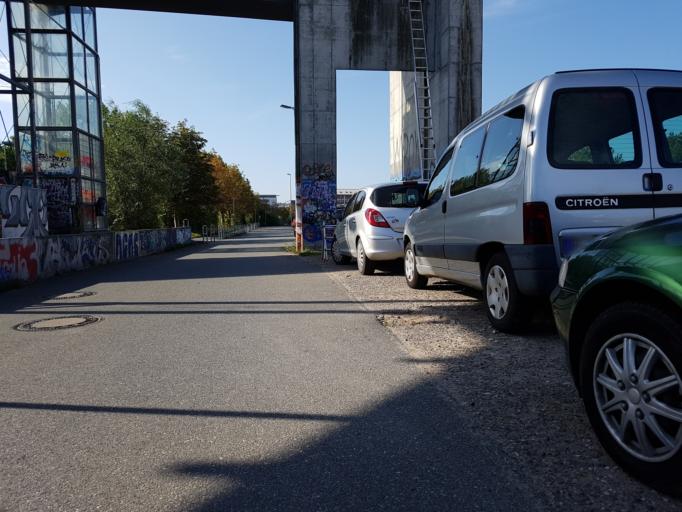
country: DE
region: Schleswig-Holstein
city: Kiel
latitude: 54.3140
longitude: 10.1398
